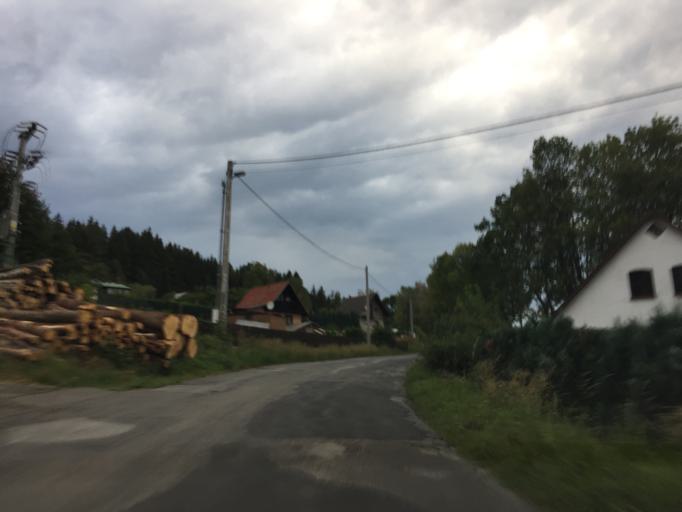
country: CZ
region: Liberecky
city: Mala Skala
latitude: 50.6619
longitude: 15.1903
